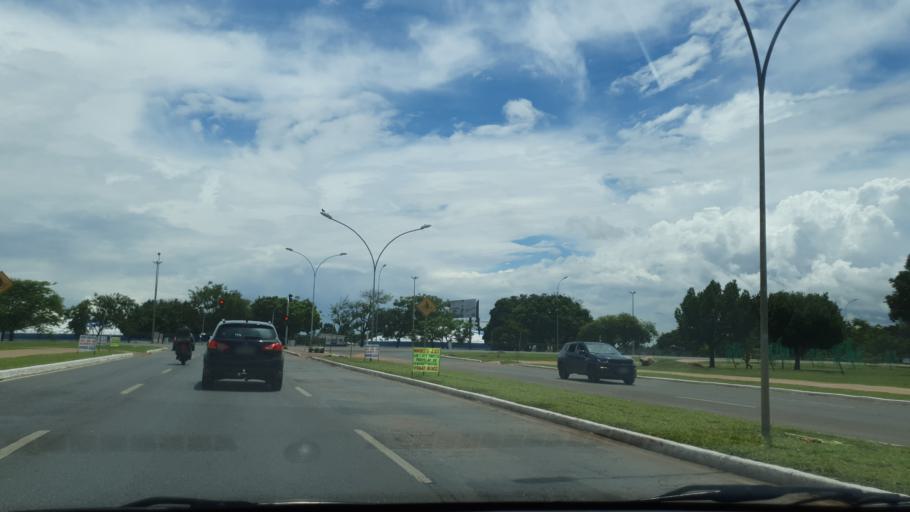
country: BR
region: Federal District
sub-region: Brasilia
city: Brasilia
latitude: -15.7835
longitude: -47.9160
